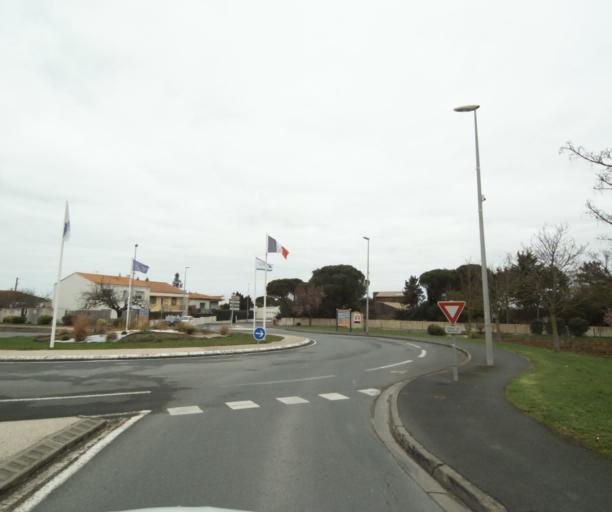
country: FR
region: Poitou-Charentes
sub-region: Departement de la Charente-Maritime
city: Nieul-sur-Mer
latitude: 46.2000
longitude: -1.1601
